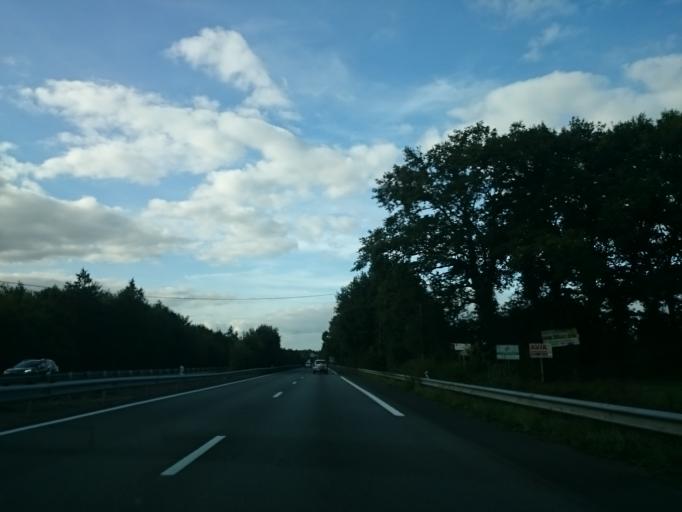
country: FR
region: Pays de la Loire
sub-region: Departement de la Loire-Atlantique
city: Derval
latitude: 47.6419
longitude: -1.6551
